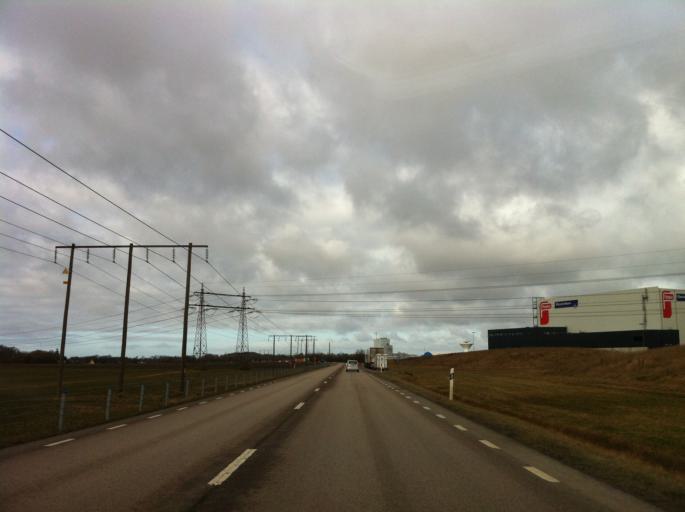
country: SE
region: Skane
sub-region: Bjuvs Kommun
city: Billesholm
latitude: 56.0464
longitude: 12.9673
